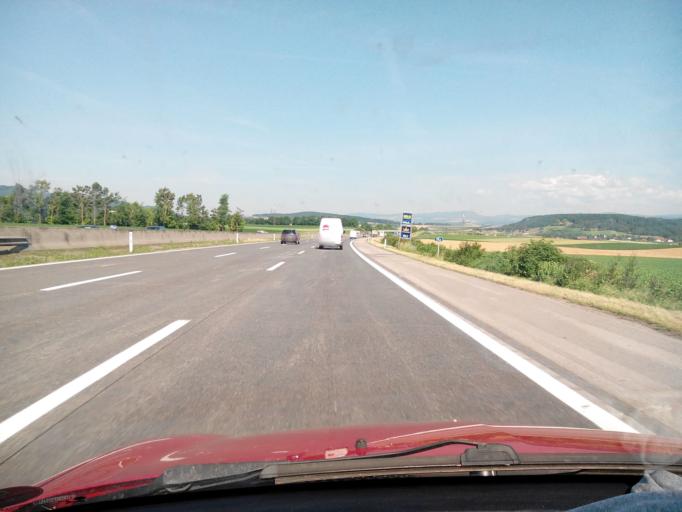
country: AT
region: Lower Austria
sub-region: Politischer Bezirk Melk
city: Loosdorf
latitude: 48.1893
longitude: 15.3980
